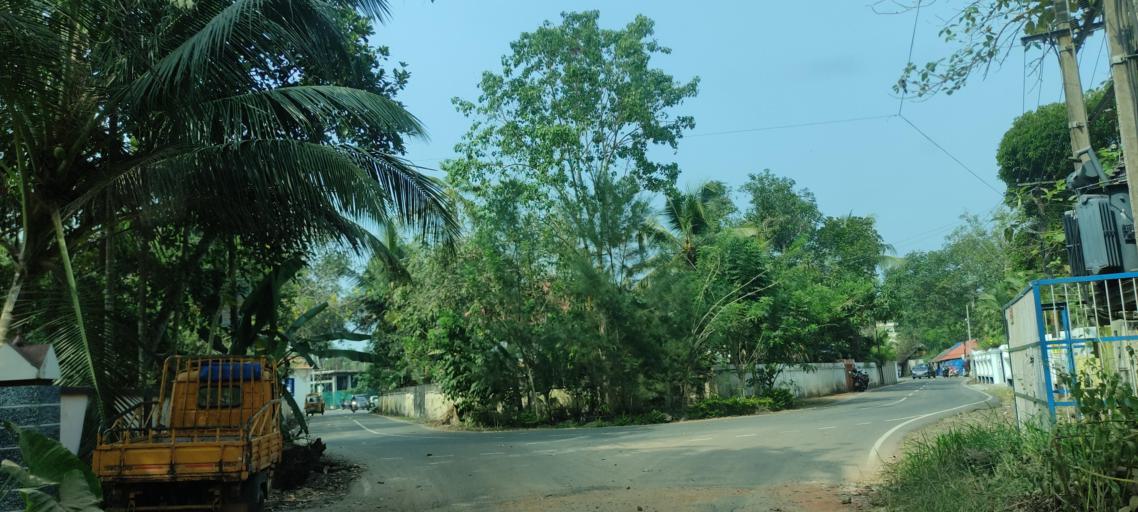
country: IN
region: Kerala
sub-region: Alappuzha
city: Shertallai
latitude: 9.6831
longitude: 76.3365
